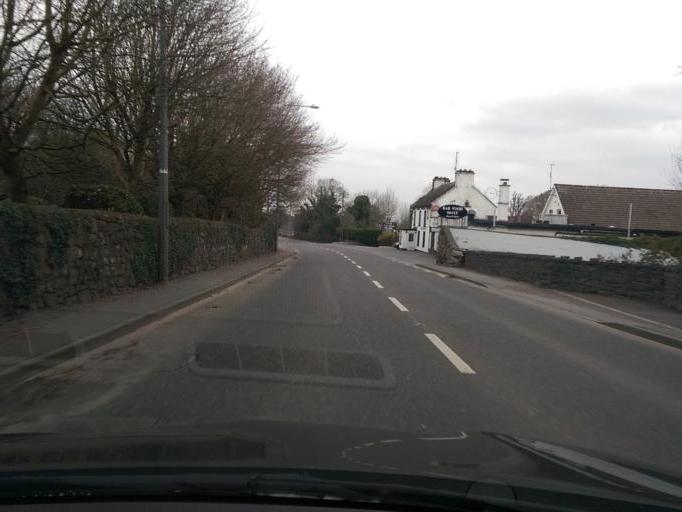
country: IE
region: Connaught
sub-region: County Galway
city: Gaillimh
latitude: 53.2960
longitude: -9.0929
